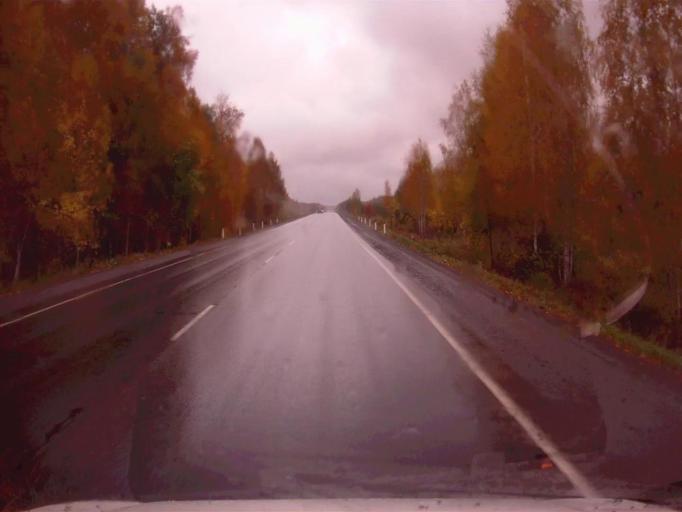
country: RU
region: Chelyabinsk
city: Argayash
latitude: 55.4361
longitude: 60.9758
